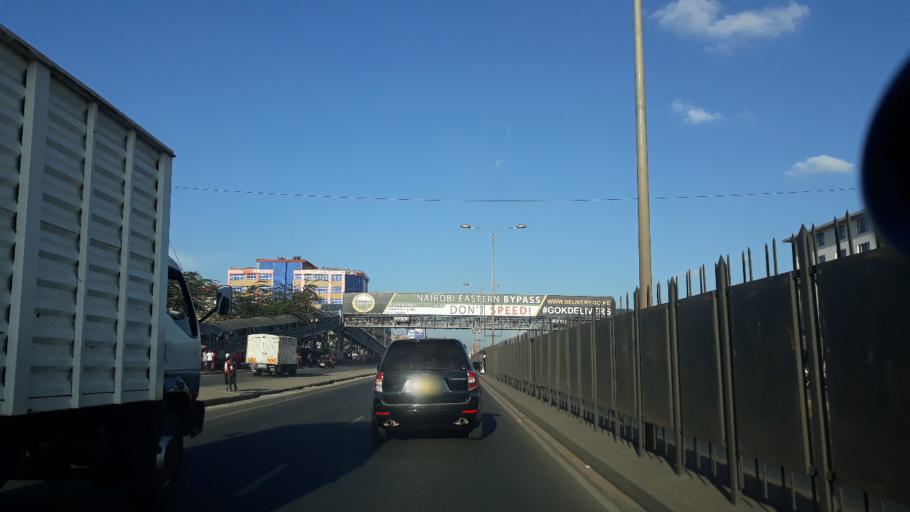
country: KE
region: Nairobi Area
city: Pumwani
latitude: -1.3280
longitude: 36.8932
